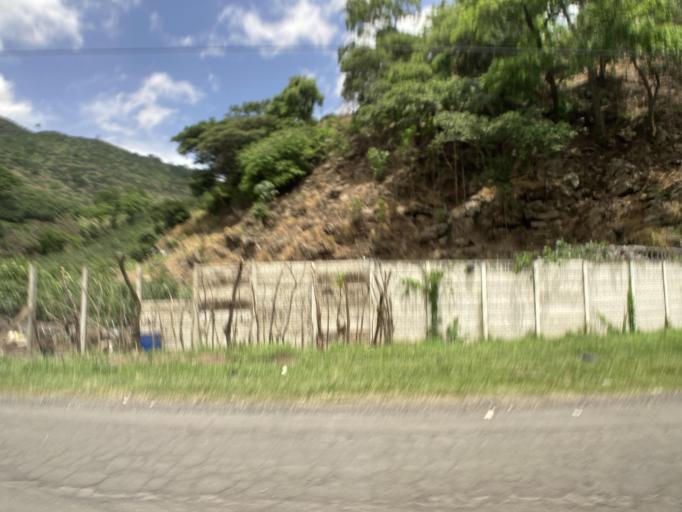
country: GT
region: Guatemala
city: Amatitlan
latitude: 14.4615
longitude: -90.5861
